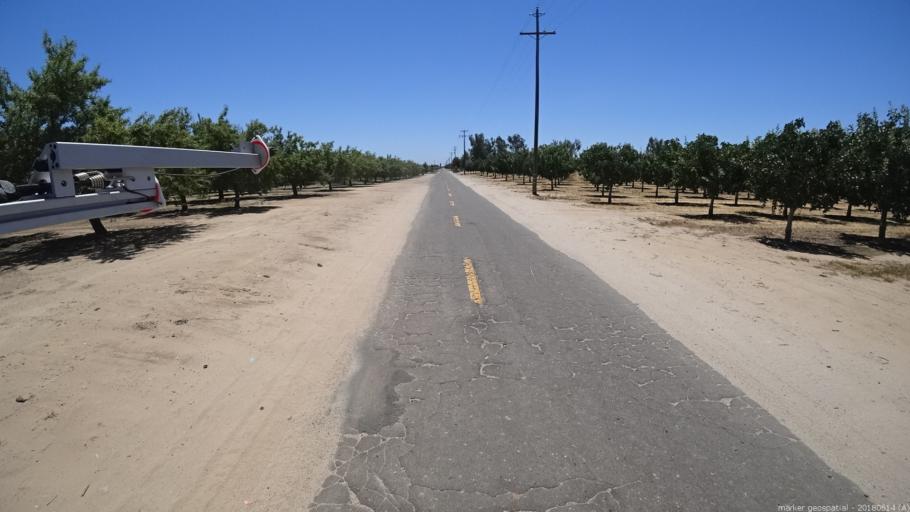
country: US
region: California
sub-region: Madera County
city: Fairmead
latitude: 37.0214
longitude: -120.1470
